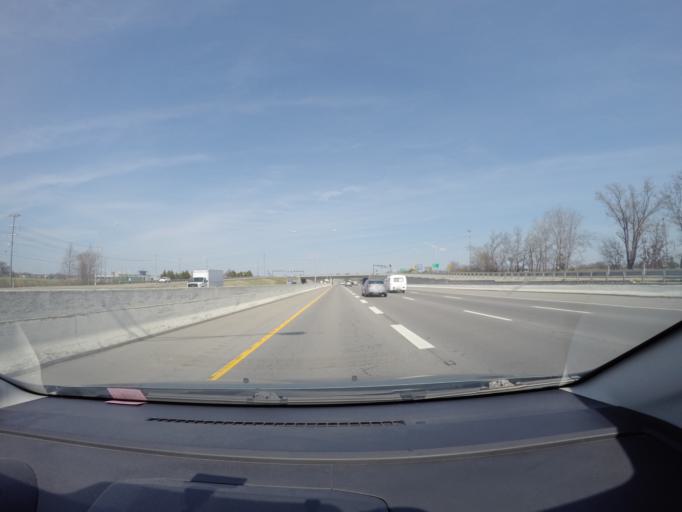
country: US
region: Tennessee
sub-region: Rutherford County
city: Murfreesboro
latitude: 35.8658
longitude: -86.4555
